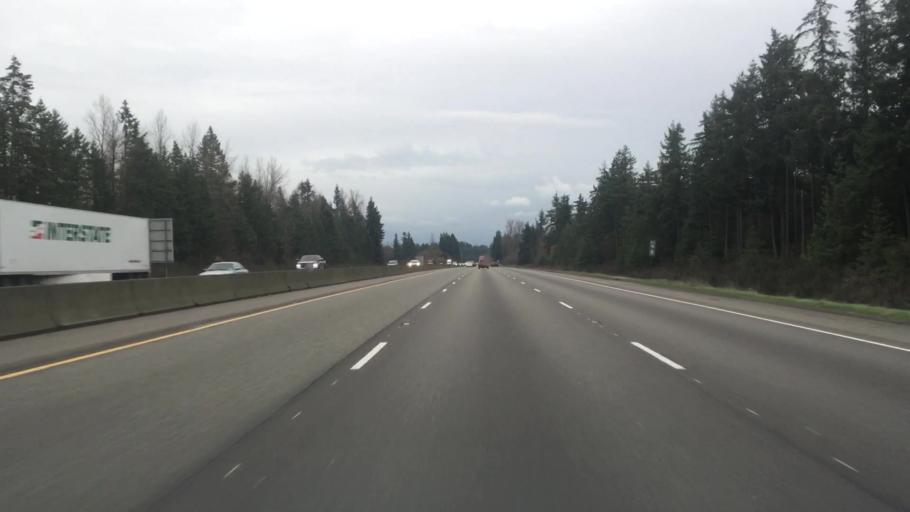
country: US
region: Washington
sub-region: Thurston County
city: Tumwater
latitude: 46.9351
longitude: -122.9428
